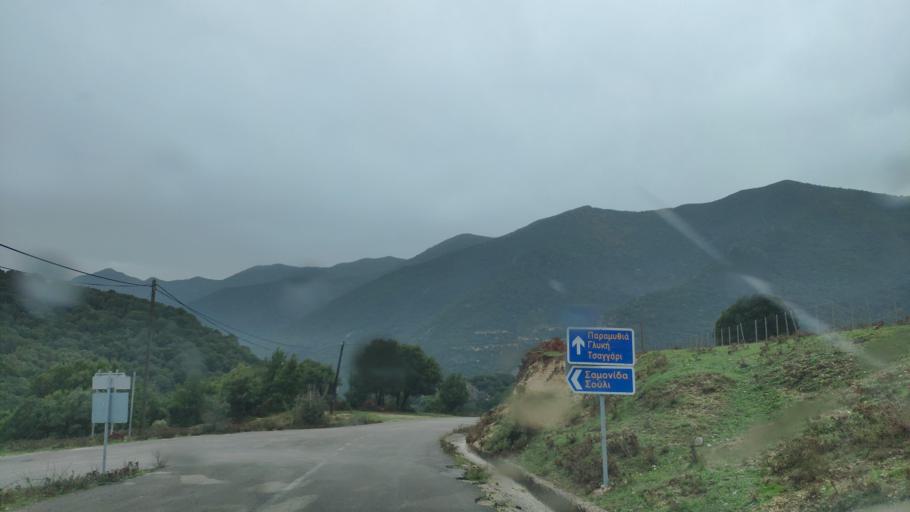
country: GR
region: Epirus
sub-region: Nomos Thesprotias
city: Paramythia
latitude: 39.4200
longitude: 20.6176
